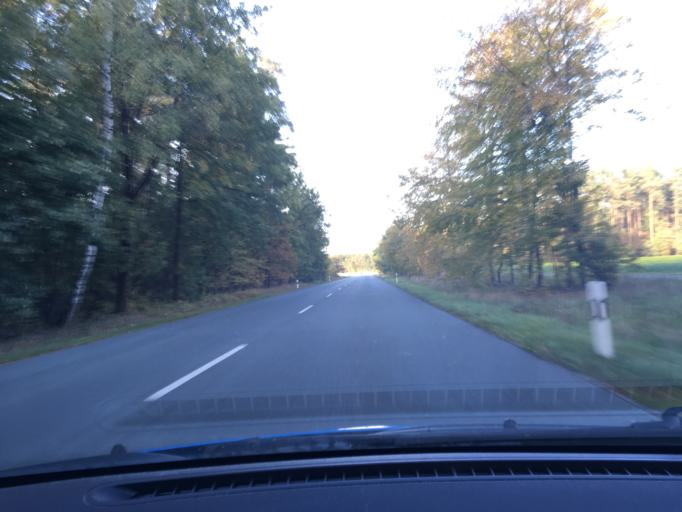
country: DE
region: Lower Saxony
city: Munster
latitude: 53.0260
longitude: 10.0565
